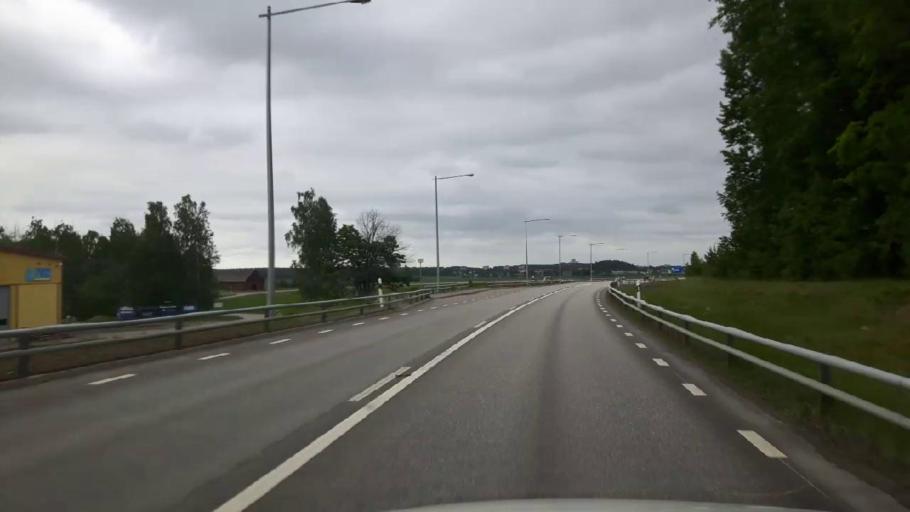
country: SE
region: Vaestmanland
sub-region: Kopings Kommun
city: Koping
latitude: 59.5372
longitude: 15.9503
